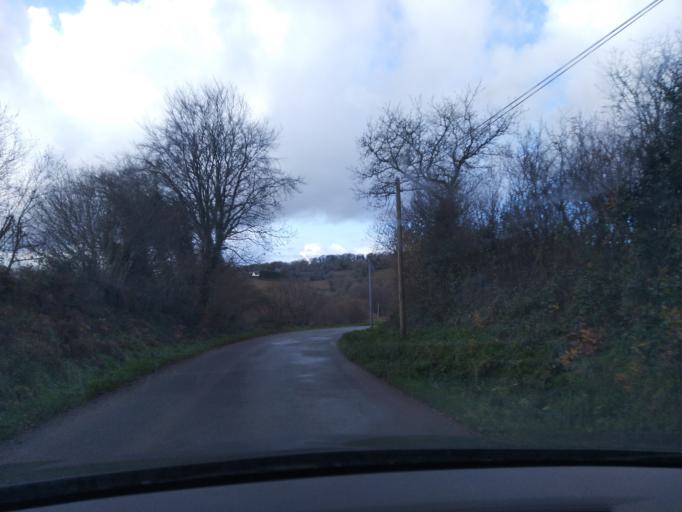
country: FR
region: Brittany
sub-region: Departement du Finistere
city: Guerlesquin
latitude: 48.4293
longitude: -3.6035
